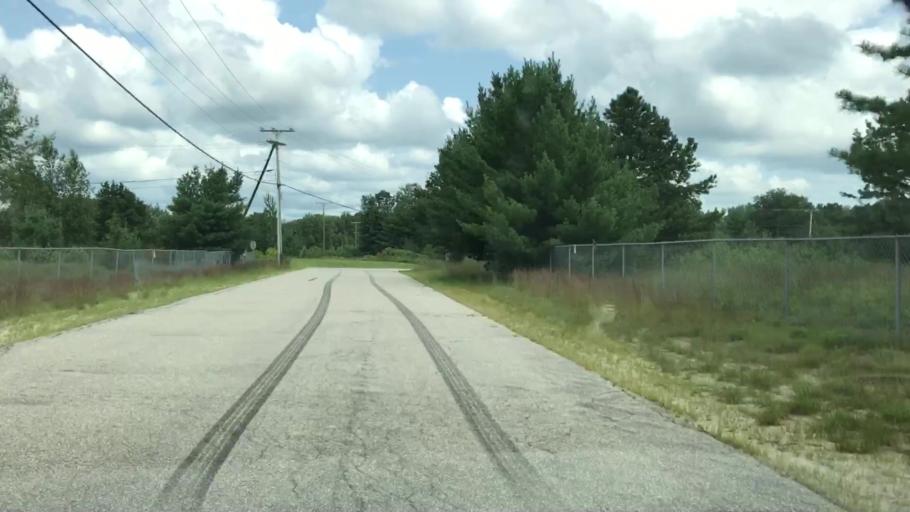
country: US
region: New Hampshire
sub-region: Hillsborough County
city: Hollis
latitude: 42.8048
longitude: -71.5864
